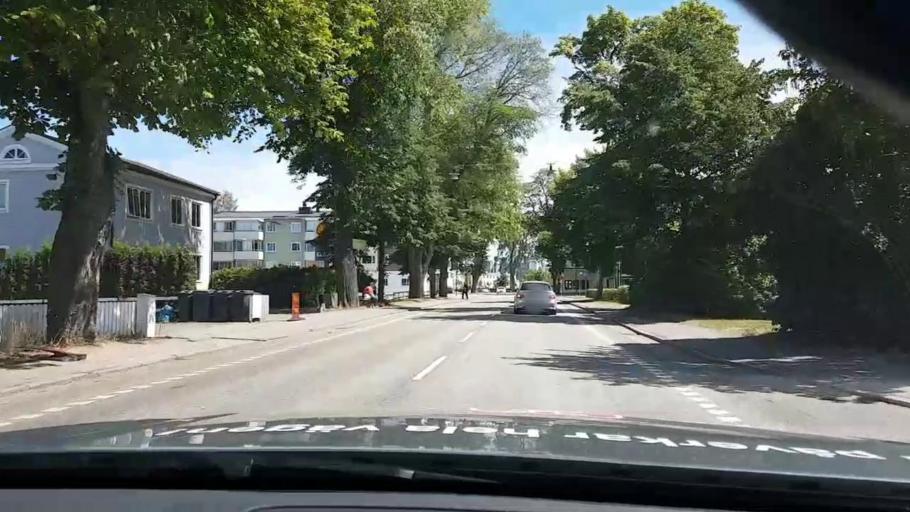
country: SE
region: Kalmar
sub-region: Vasterviks Kommun
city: Vaestervik
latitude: 57.7574
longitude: 16.6270
